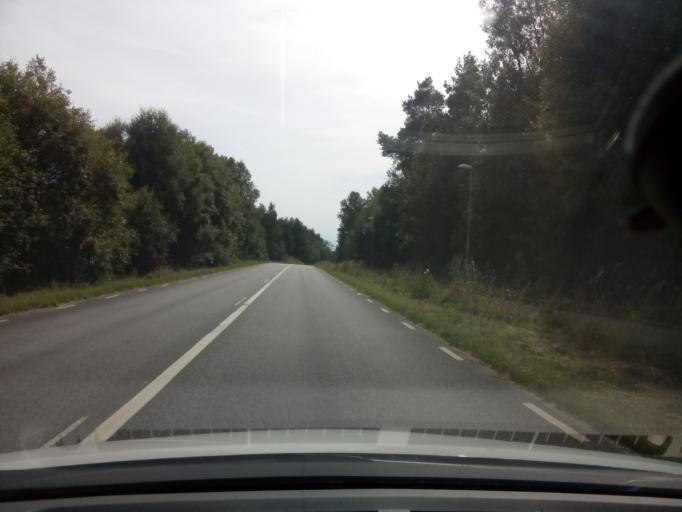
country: SE
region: Soedermanland
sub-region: Nykopings Kommun
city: Nykoping
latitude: 58.7715
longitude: 17.0711
